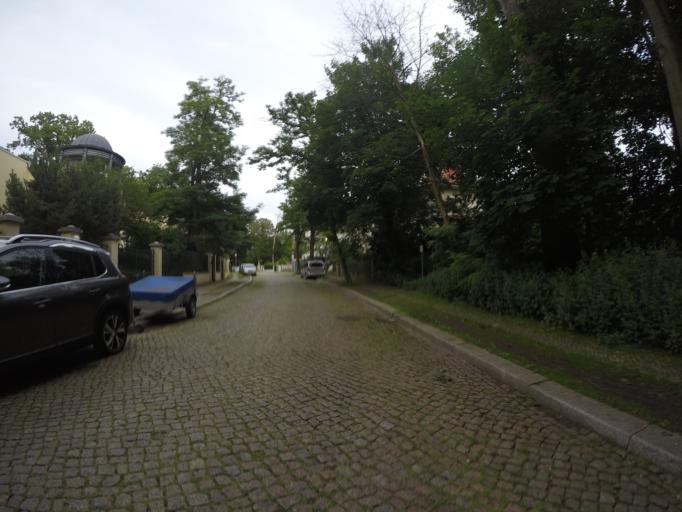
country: DE
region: Berlin
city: Grunewald
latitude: 52.4794
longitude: 13.2657
